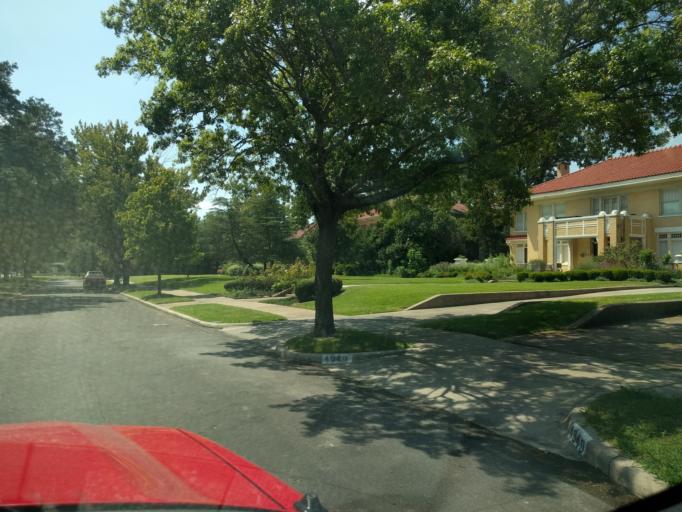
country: US
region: Texas
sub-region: Dallas County
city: Highland Park
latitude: 32.8026
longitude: -96.7694
